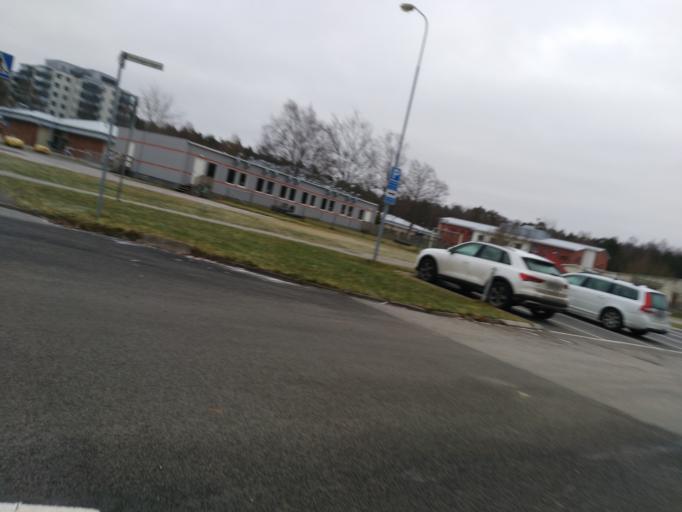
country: SE
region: Vaestra Goetaland
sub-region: Lidkopings Kommun
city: Lidkoping
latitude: 58.4908
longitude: 13.1549
